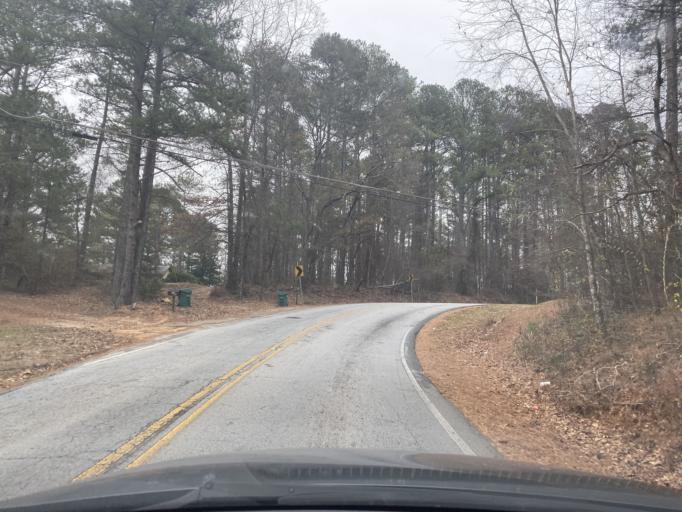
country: US
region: Georgia
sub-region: DeKalb County
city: Pine Mountain
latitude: 33.6906
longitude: -84.1581
